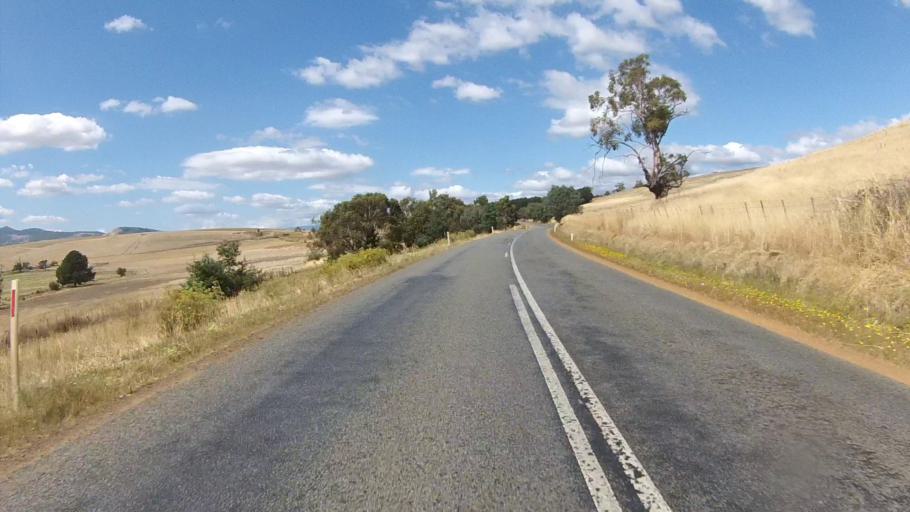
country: AU
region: Tasmania
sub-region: Derwent Valley
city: New Norfolk
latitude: -42.6851
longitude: 146.8692
